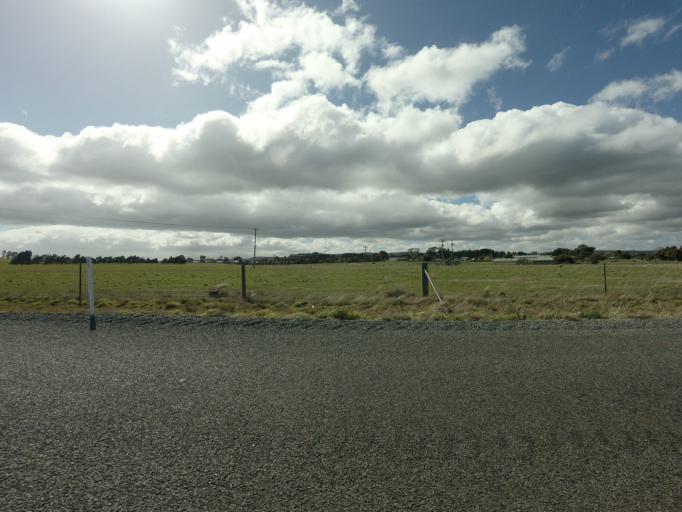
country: AU
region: Tasmania
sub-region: Northern Midlands
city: Evandale
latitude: -41.9207
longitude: 147.4813
